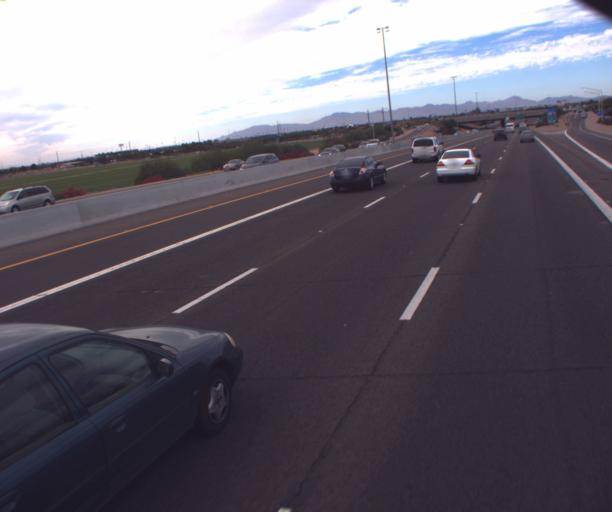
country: US
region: Arizona
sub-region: Maricopa County
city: Chandler
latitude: 33.2828
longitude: -111.8187
